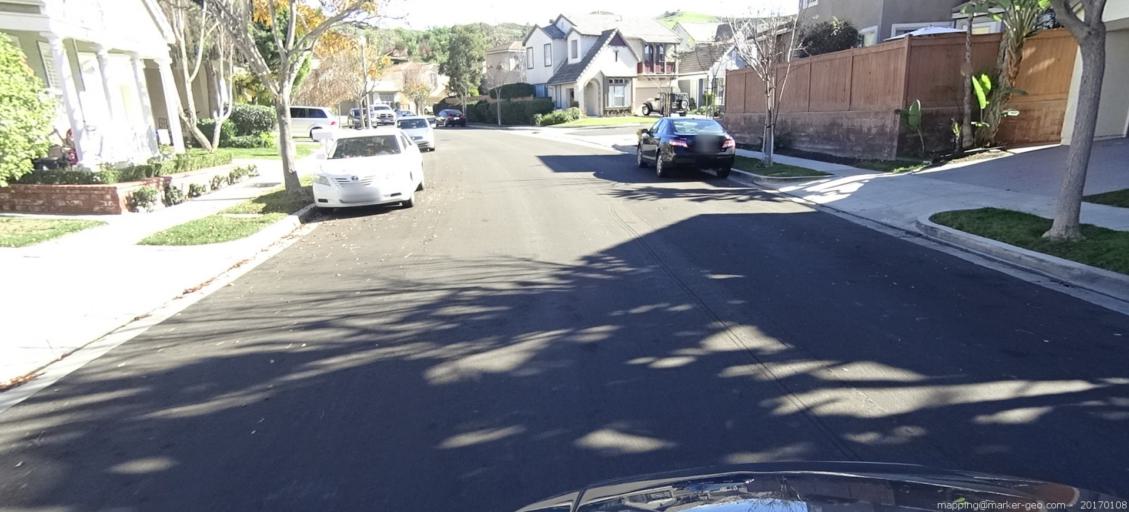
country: US
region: California
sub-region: Orange County
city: Ladera Ranch
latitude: 33.5673
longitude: -117.6310
